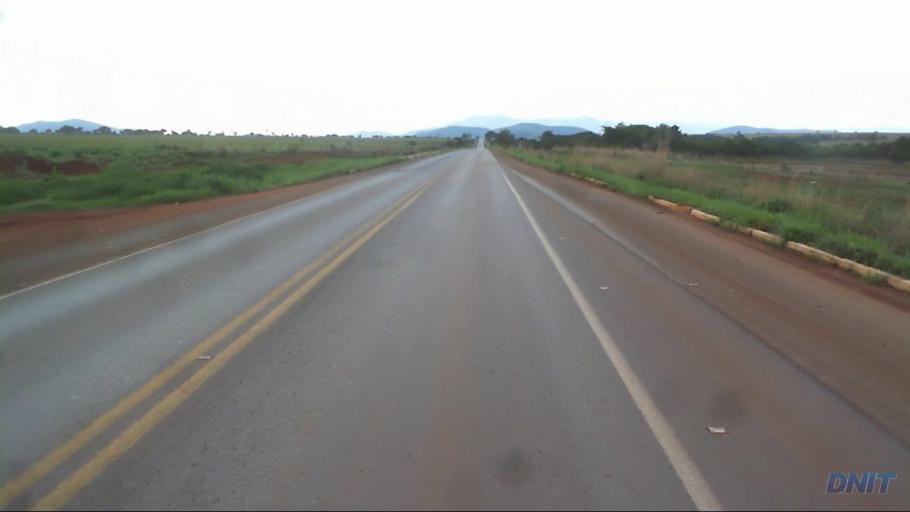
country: BR
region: Goias
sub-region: Barro Alto
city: Barro Alto
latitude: -14.8396
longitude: -49.0304
